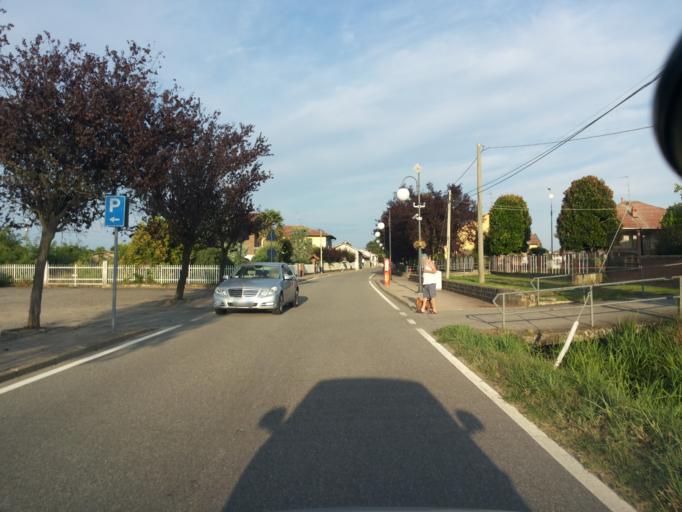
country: IT
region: Piedmont
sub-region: Provincia di Vercelli
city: Salasco
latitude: 45.3258
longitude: 8.2603
